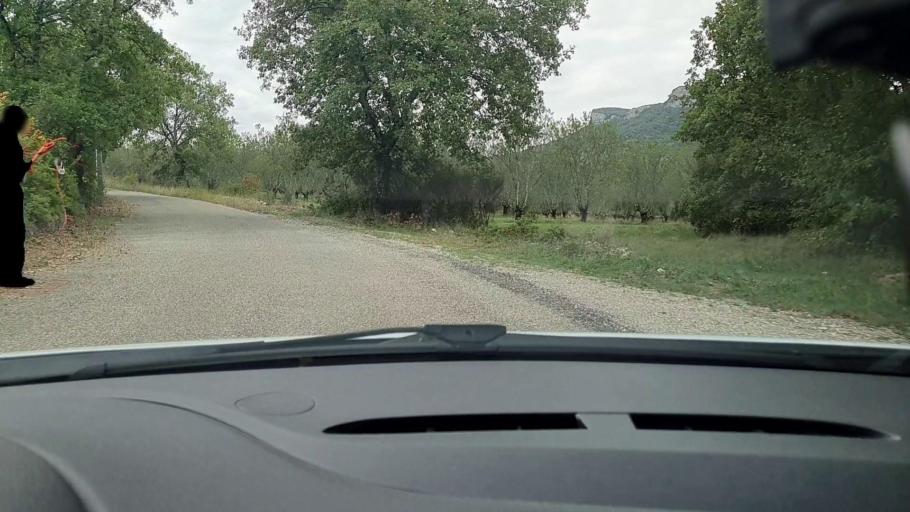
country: FR
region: Languedoc-Roussillon
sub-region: Departement du Gard
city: Mons
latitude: 44.1612
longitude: 4.2853
